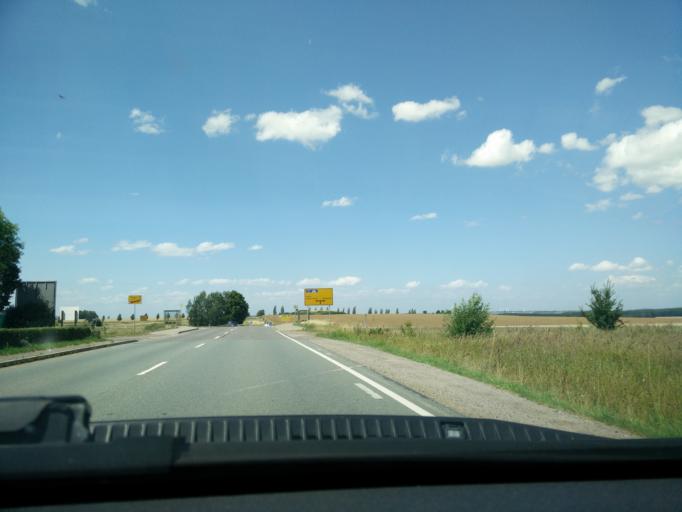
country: DE
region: Saxony
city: Muhlau
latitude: 50.9060
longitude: 12.7521
